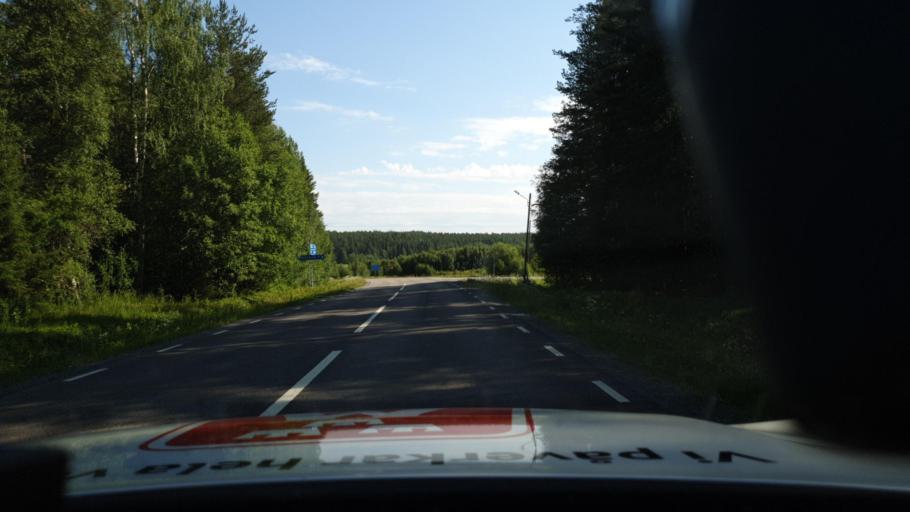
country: SE
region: Norrbotten
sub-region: Lulea Kommun
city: Sodra Sunderbyn
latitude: 65.8285
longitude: 21.9412
